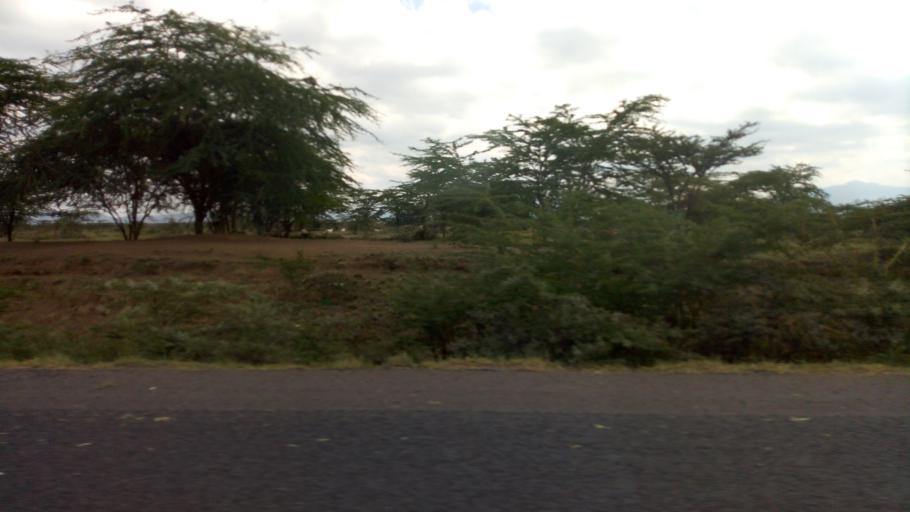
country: KE
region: Nakuru
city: Kijabe
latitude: -1.0317
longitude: 36.3945
